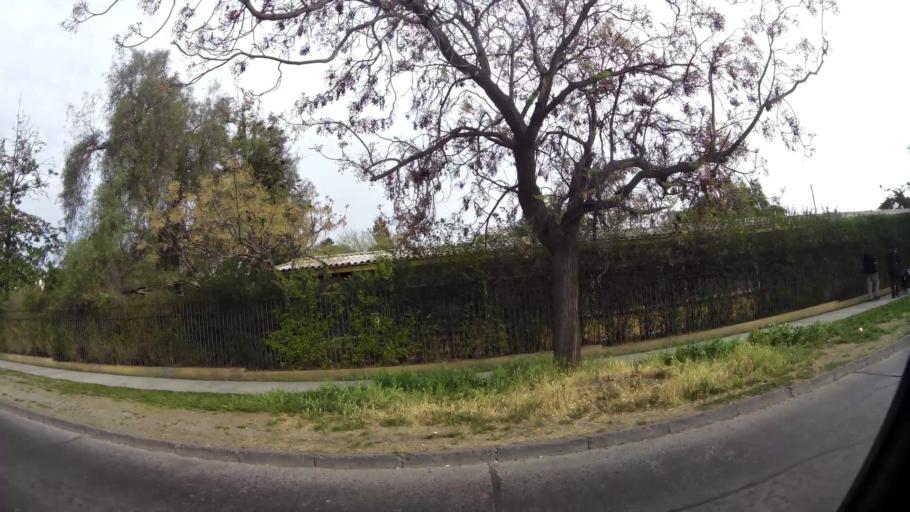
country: CL
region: Santiago Metropolitan
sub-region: Provincia de Santiago
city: Lo Prado
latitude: -33.5160
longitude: -70.7538
